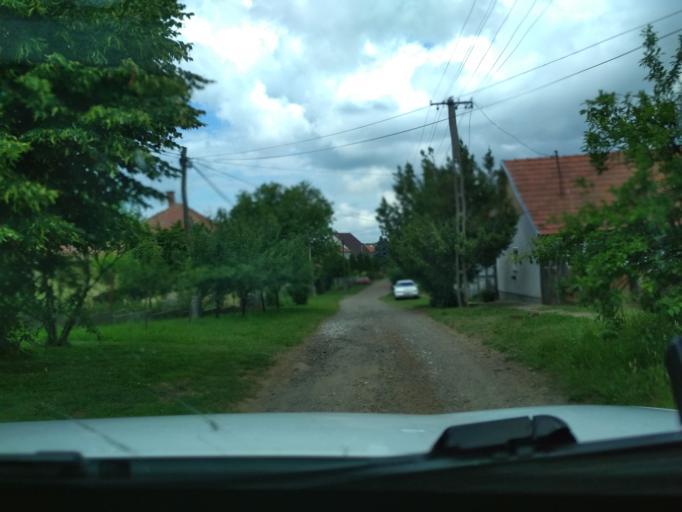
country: HU
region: Jasz-Nagykun-Szolnok
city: Tiszafured
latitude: 47.6096
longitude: 20.7474
